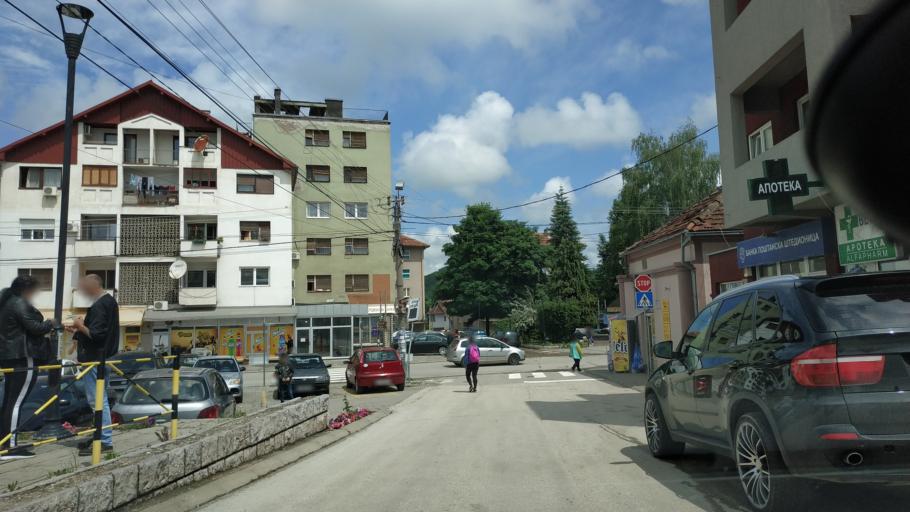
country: RS
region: Central Serbia
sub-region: Zajecarski Okrug
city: Boljevac
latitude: 43.8301
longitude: 21.9588
